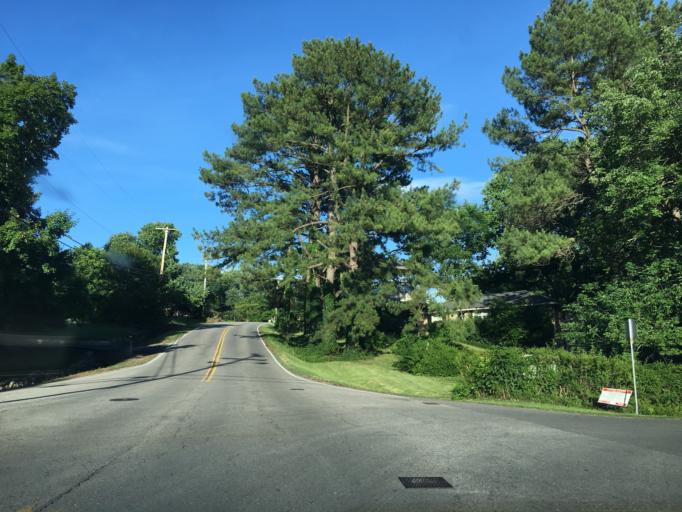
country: US
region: Tennessee
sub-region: Davidson County
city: Oak Hill
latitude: 36.0630
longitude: -86.7354
